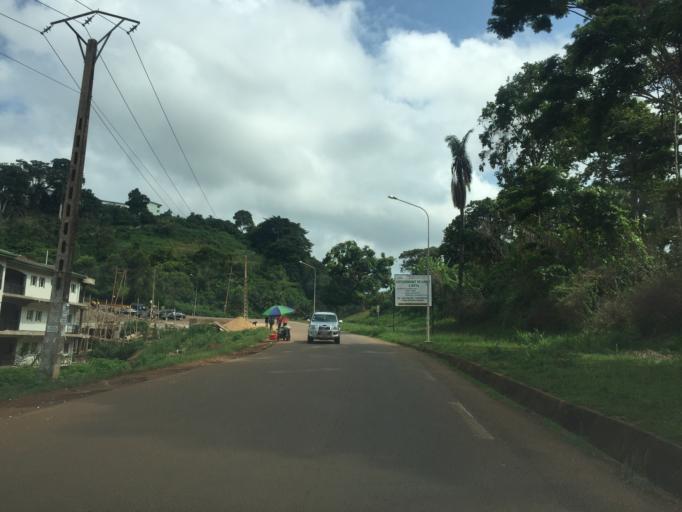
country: CM
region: Centre
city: Yaounde
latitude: 3.9140
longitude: 11.5019
